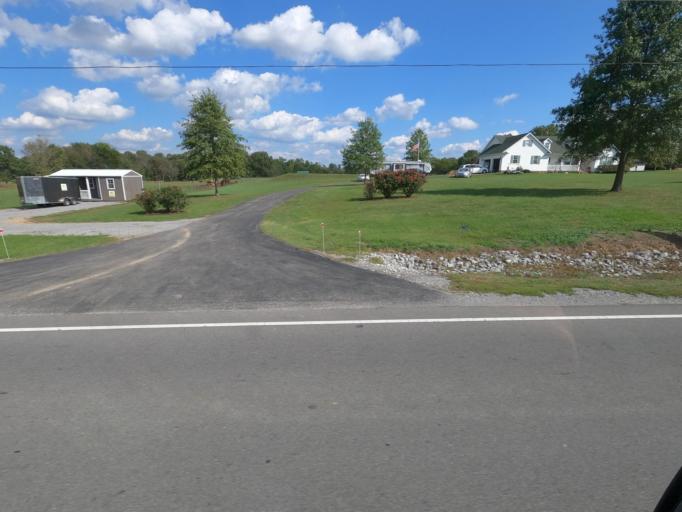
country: US
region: Illinois
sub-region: Massac County
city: Metropolis
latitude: 37.1713
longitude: -88.6766
